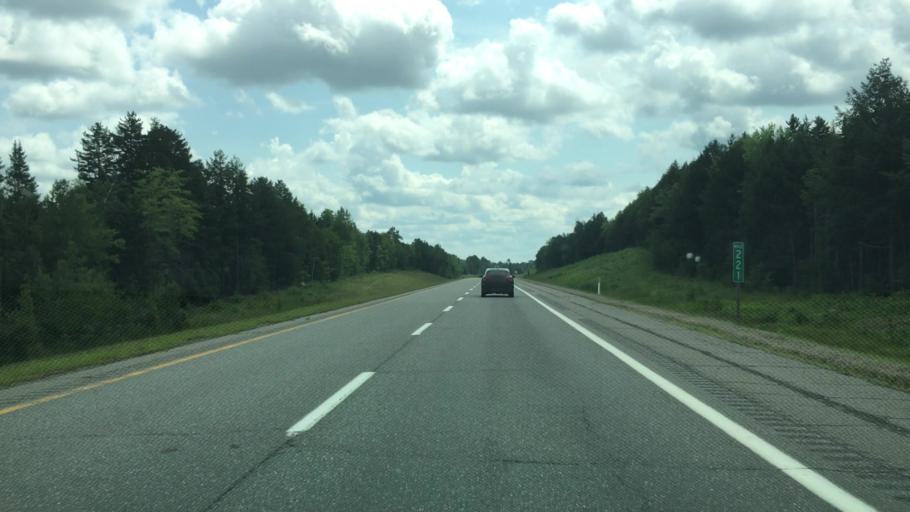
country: US
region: Maine
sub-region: Penobscot County
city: Howland
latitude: 45.2974
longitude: -68.6637
